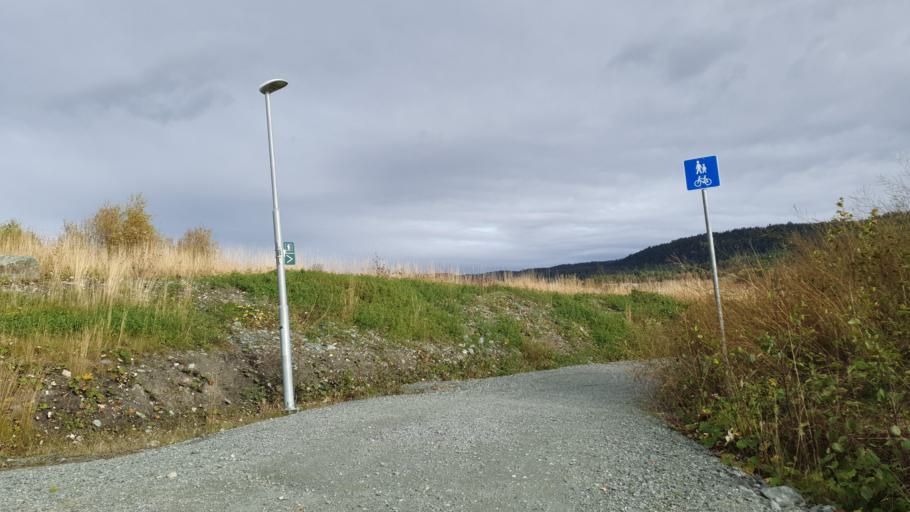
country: NO
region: Sor-Trondelag
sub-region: Klaebu
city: Klaebu
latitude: 63.3048
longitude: 10.4693
